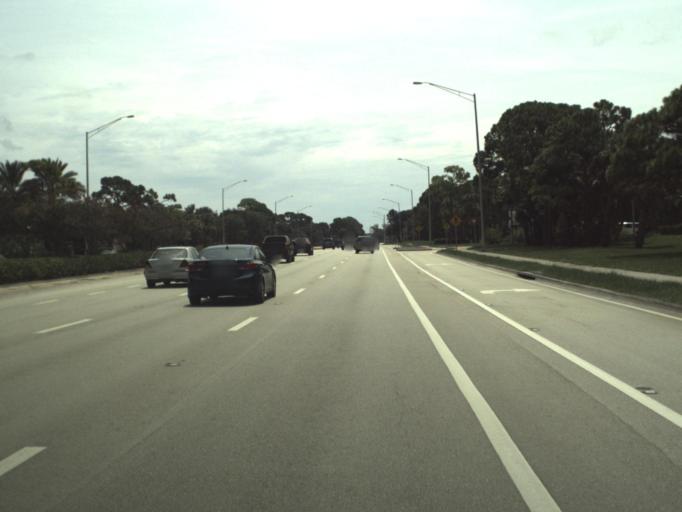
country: US
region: Florida
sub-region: Palm Beach County
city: North Palm Beach
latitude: 26.8448
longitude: -80.0808
